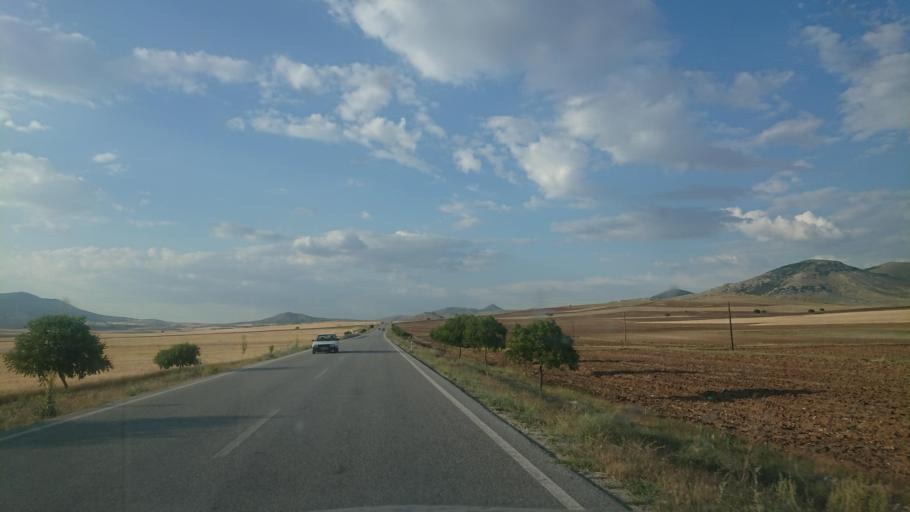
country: TR
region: Aksaray
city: Aksaray
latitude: 38.5260
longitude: 34.0951
